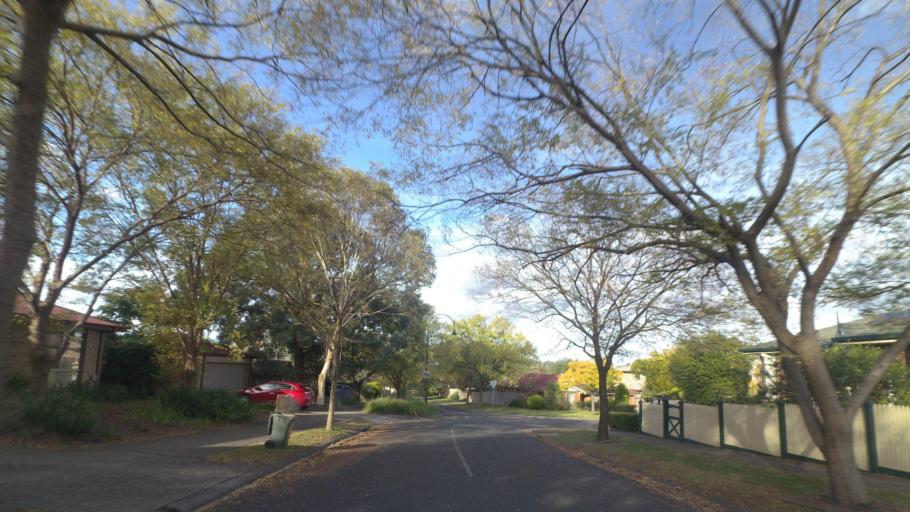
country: AU
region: Victoria
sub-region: Banyule
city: Yallambie
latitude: -37.7260
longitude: 145.0979
